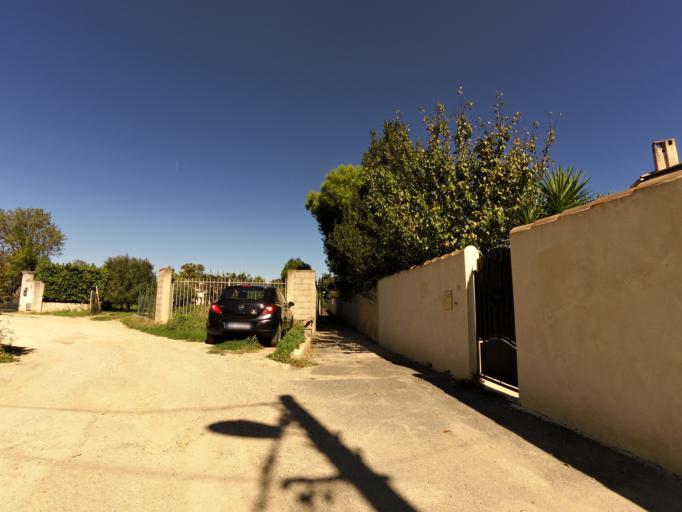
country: FR
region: Languedoc-Roussillon
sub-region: Departement du Gard
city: Codognan
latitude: 43.7314
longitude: 4.2211
